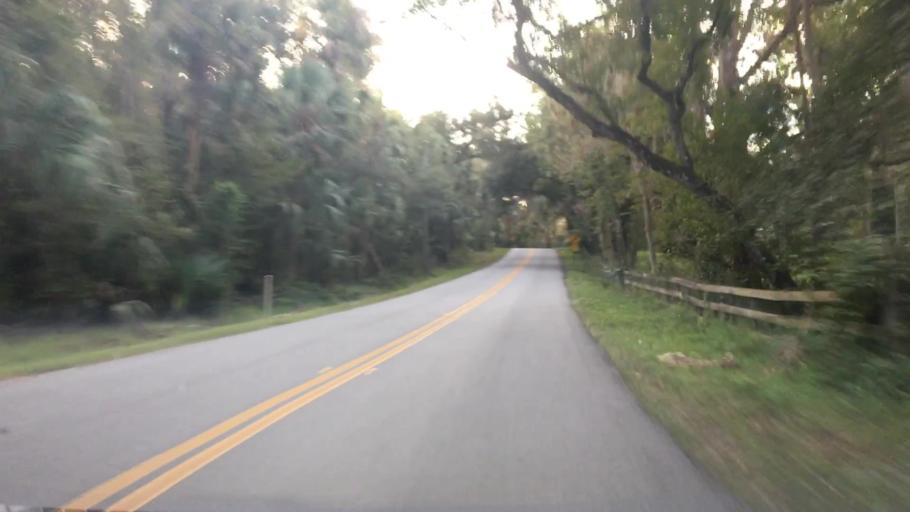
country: US
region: Florida
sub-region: Seminole County
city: Midway
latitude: 28.8541
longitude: -81.2071
